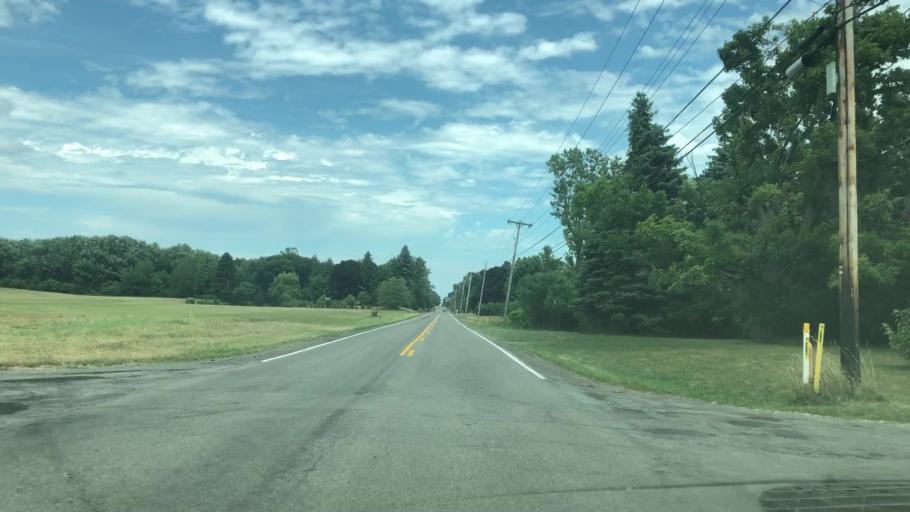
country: US
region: New York
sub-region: Monroe County
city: Webster
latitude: 43.1741
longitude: -77.4005
